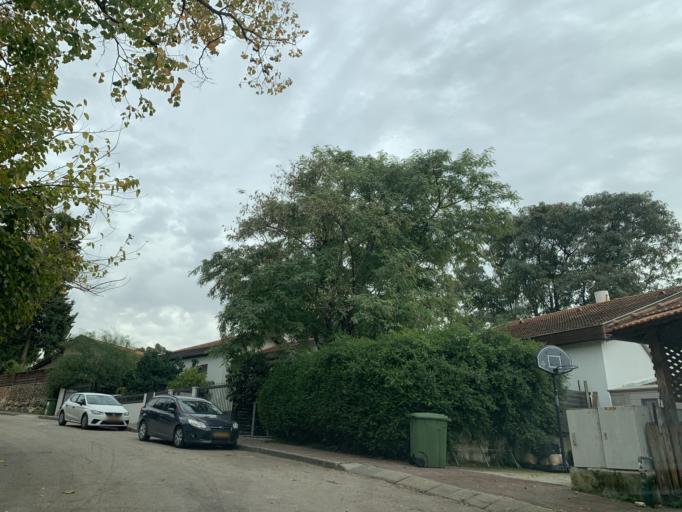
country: IL
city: Nirit
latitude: 32.1461
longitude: 34.9826
